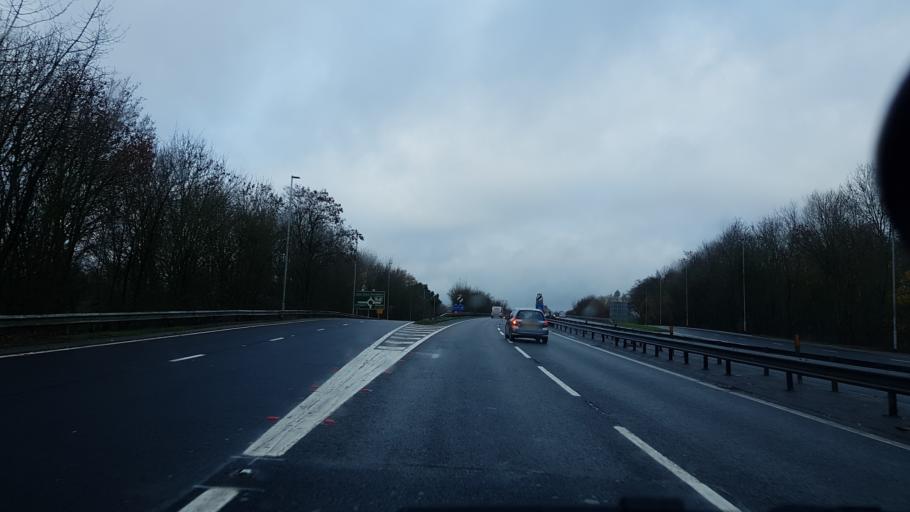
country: GB
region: England
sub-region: Bracknell Forest
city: Binfield
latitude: 51.4106
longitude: -0.7953
